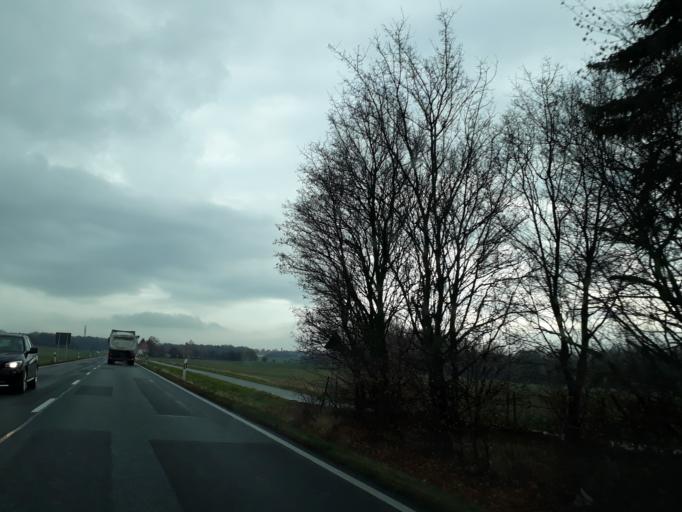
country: DE
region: Saxony
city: Hochkirch
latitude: 51.1372
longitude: 14.5983
